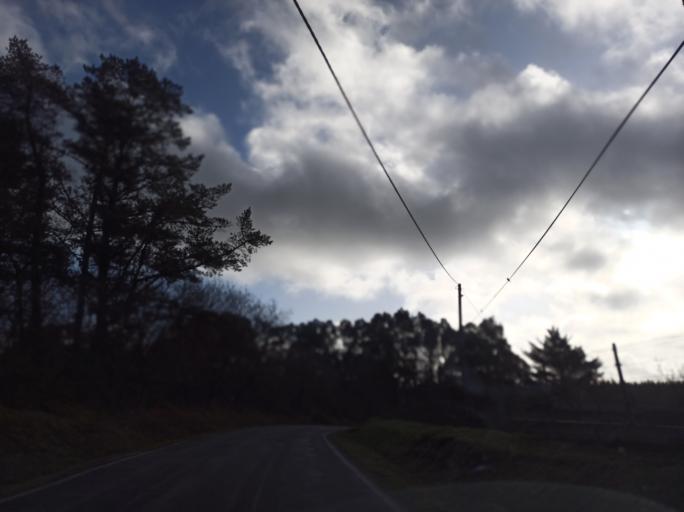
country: ES
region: Galicia
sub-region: Provincia da Coruna
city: Curtis
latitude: 43.0979
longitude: -7.9814
